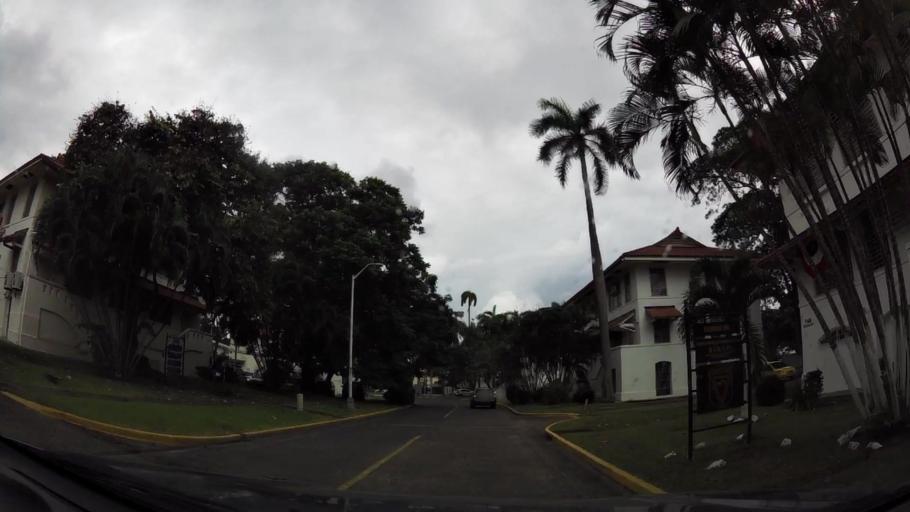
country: PA
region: Panama
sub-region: Distrito de Panama
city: Ancon
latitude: 8.9554
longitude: -79.5570
